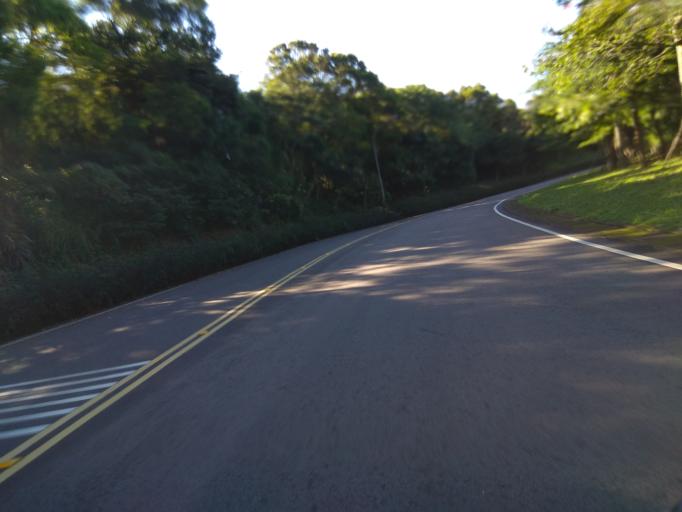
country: TW
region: Taiwan
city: Daxi
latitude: 24.8933
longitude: 121.1491
